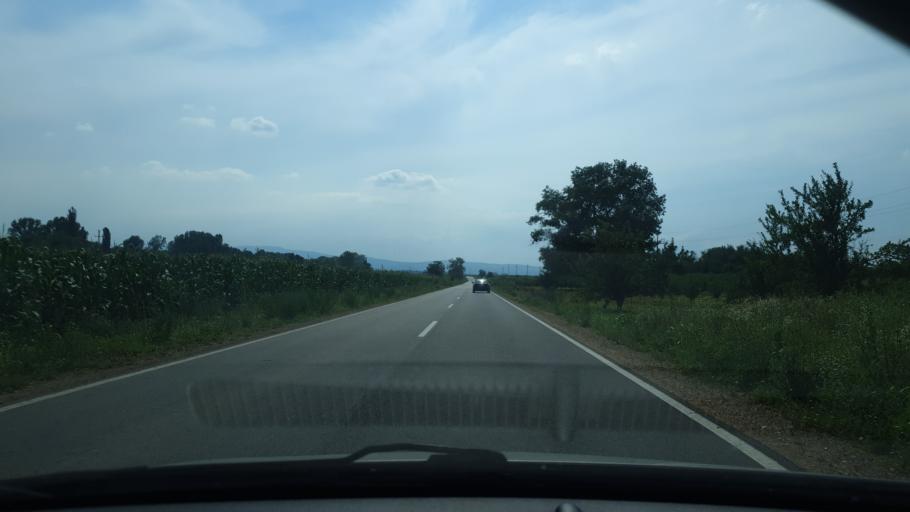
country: RS
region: Central Serbia
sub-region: Pomoravski Okrug
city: Cuprija
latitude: 43.9549
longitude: 21.4561
